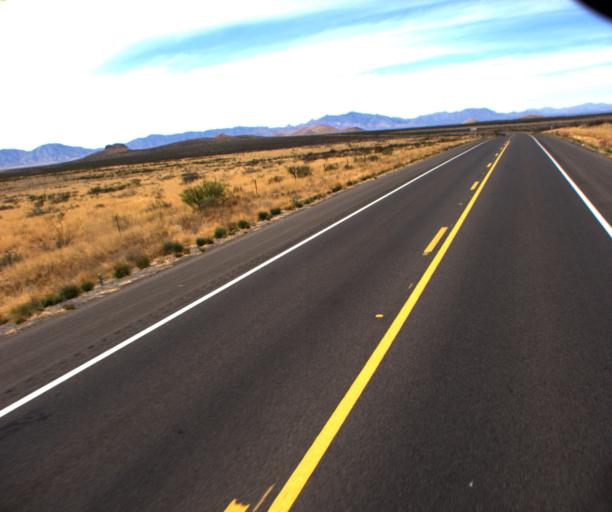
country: US
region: Arizona
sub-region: Cochise County
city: Willcox
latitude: 31.9019
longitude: -109.7118
